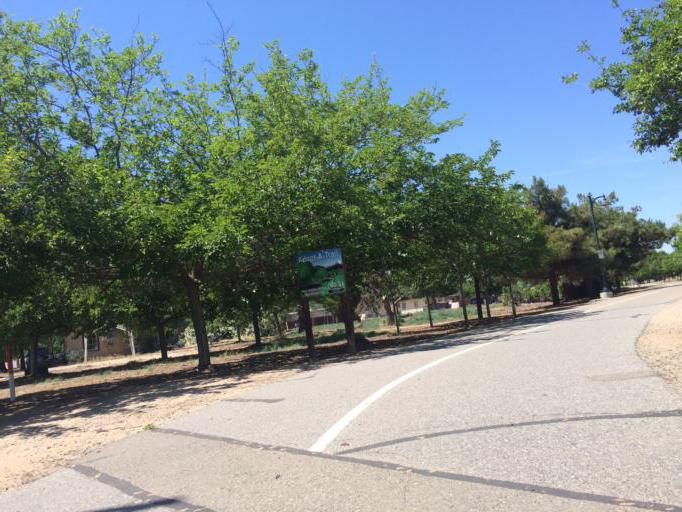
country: US
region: California
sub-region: Fresno County
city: Clovis
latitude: 36.8303
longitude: -119.7006
